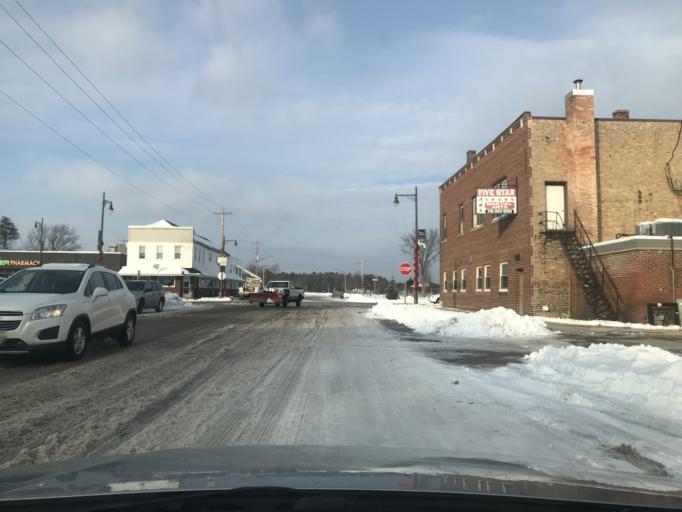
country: US
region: Wisconsin
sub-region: Marinette County
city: Peshtigo
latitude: 45.0539
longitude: -87.7491
